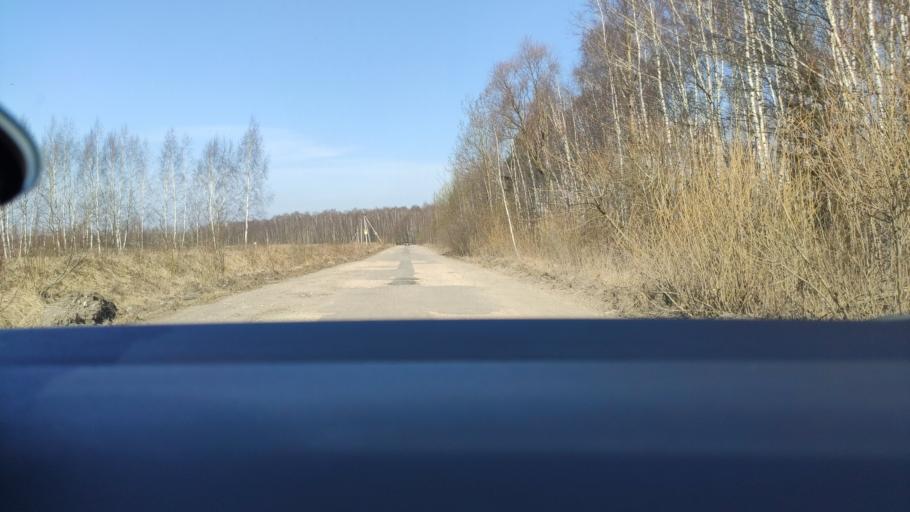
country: RU
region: Moskovskaya
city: Elektrostal'
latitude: 55.7713
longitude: 38.3823
